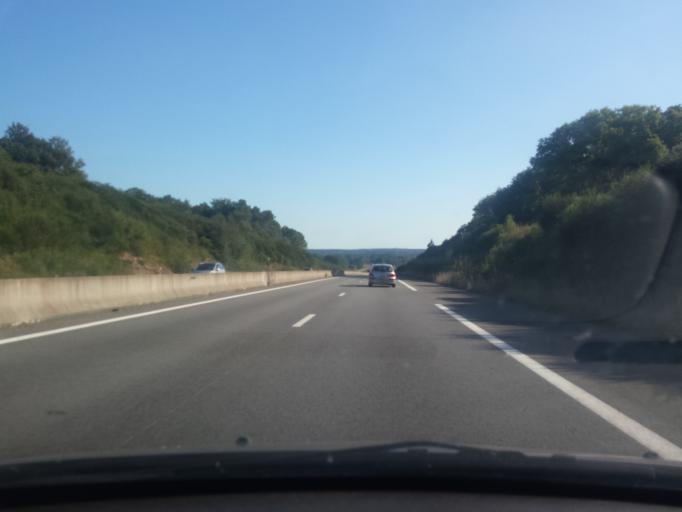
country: FR
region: Brittany
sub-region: Departement du Morbihan
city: Colpo
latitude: 47.7949
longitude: -2.8036
